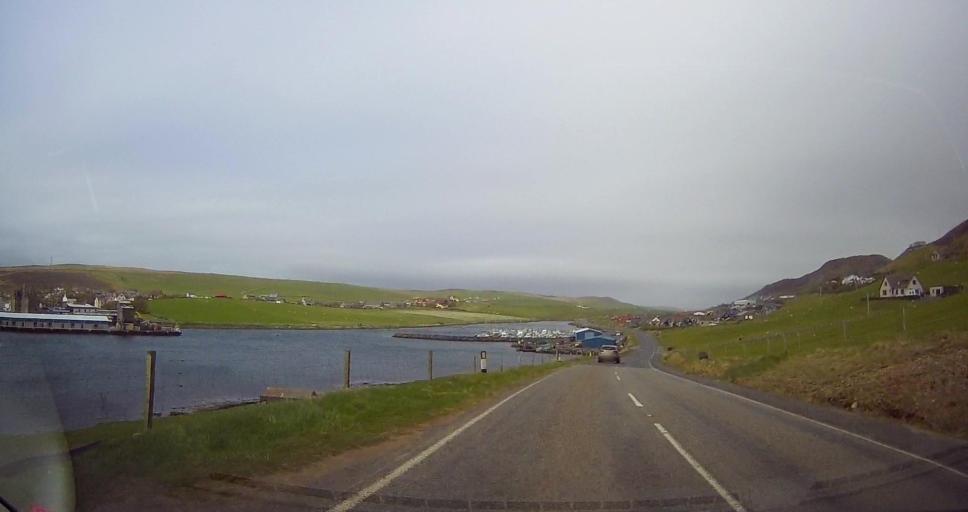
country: GB
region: Scotland
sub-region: Shetland Islands
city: Lerwick
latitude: 60.1328
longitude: -1.2671
